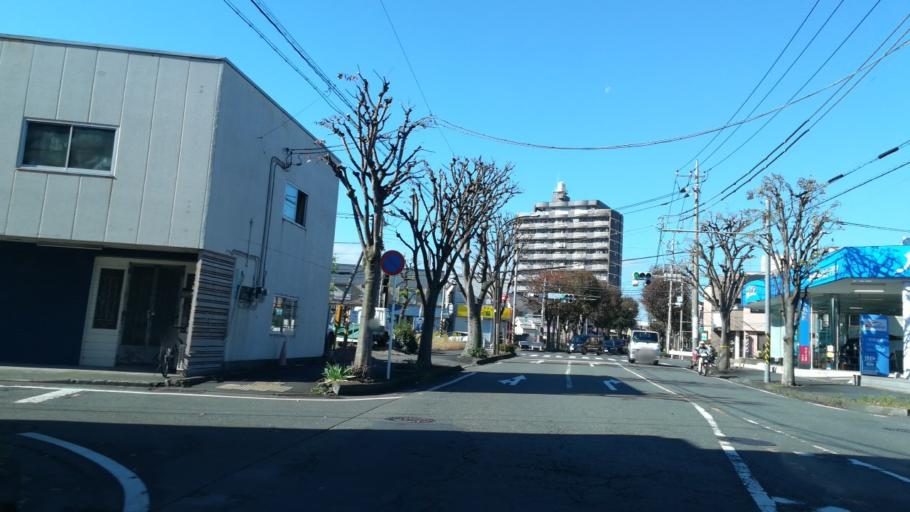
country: JP
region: Kanagawa
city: Zama
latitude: 35.5633
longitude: 139.3744
